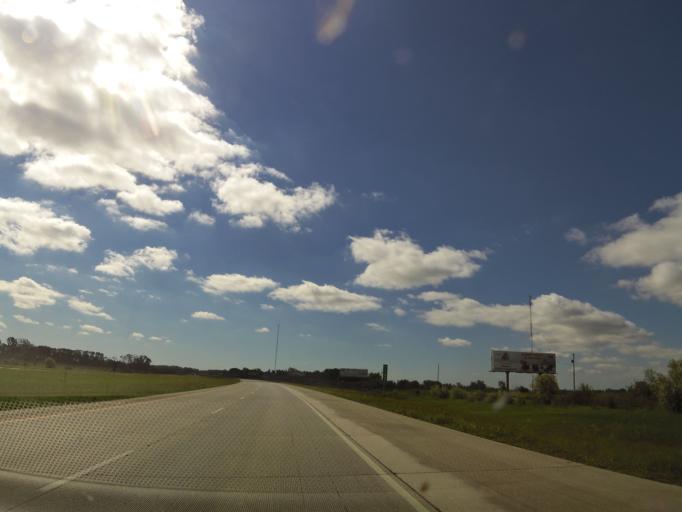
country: US
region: North Dakota
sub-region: Grand Forks County
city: Grand Forks
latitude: 48.0103
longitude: -97.1164
